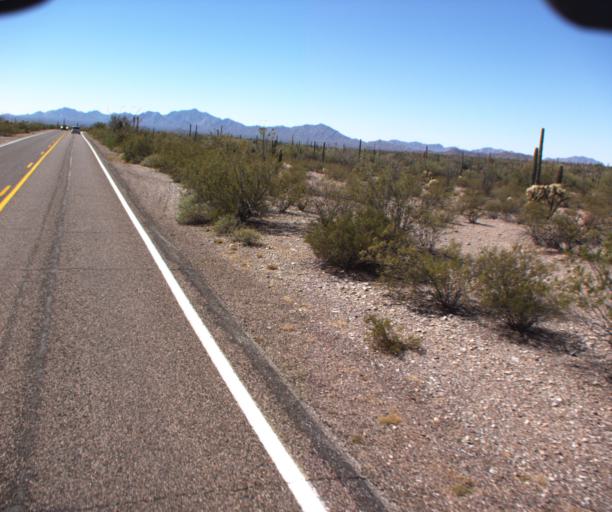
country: MX
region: Sonora
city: Sonoyta
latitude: 31.9418
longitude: -112.7989
